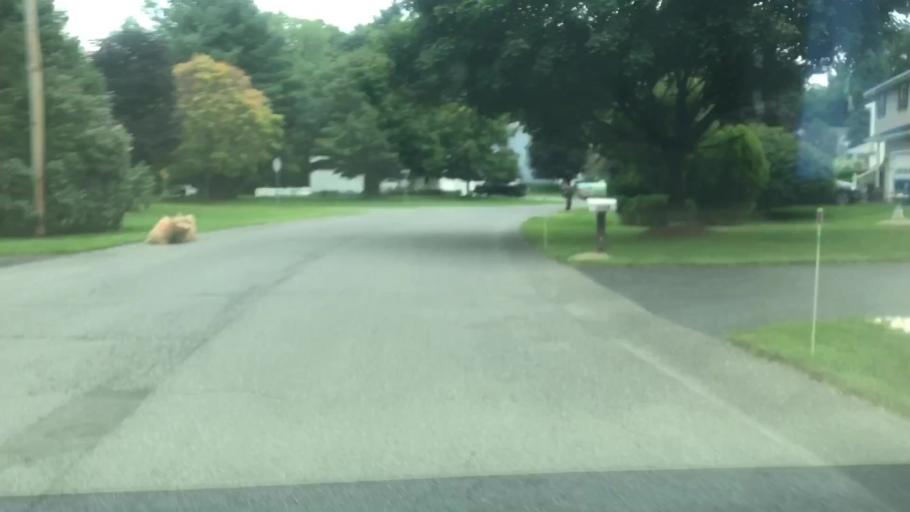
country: US
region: New York
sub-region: Albany County
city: Westmere
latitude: 42.7310
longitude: -73.9228
